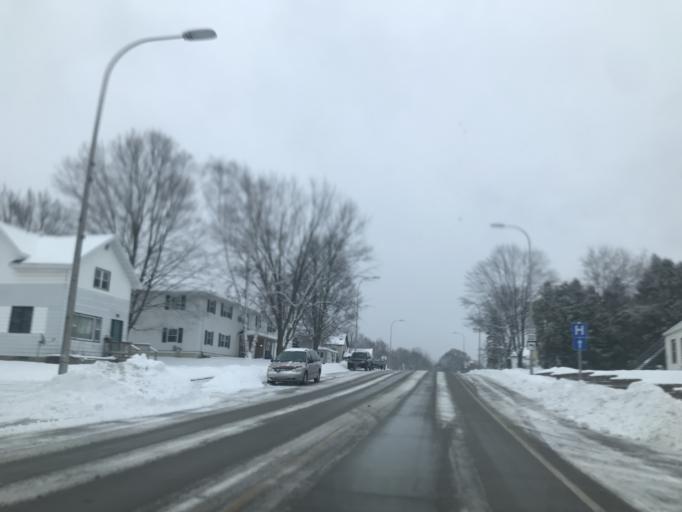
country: US
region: Wisconsin
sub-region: Oconto County
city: Oconto Falls
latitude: 44.8739
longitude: -88.1425
